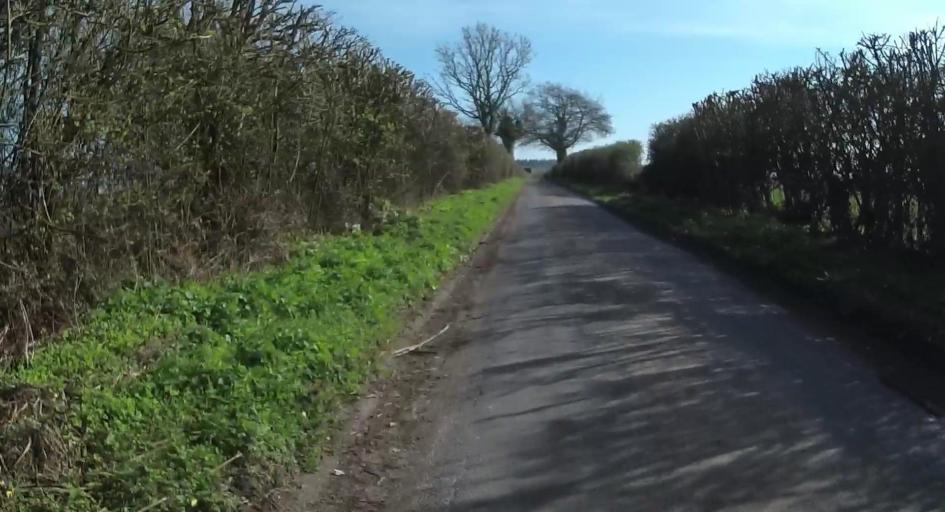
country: GB
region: England
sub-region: Hampshire
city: Highclere
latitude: 51.2511
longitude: -1.3675
